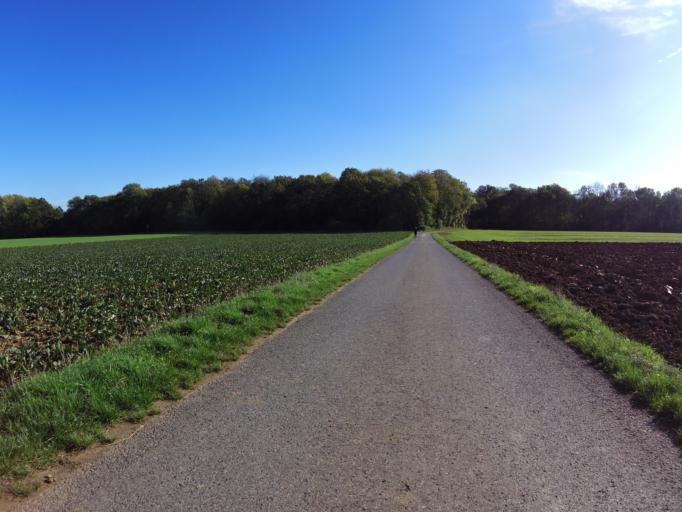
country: DE
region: Bavaria
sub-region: Regierungsbezirk Unterfranken
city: Sulzfeld am Main
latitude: 49.7236
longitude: 10.0961
